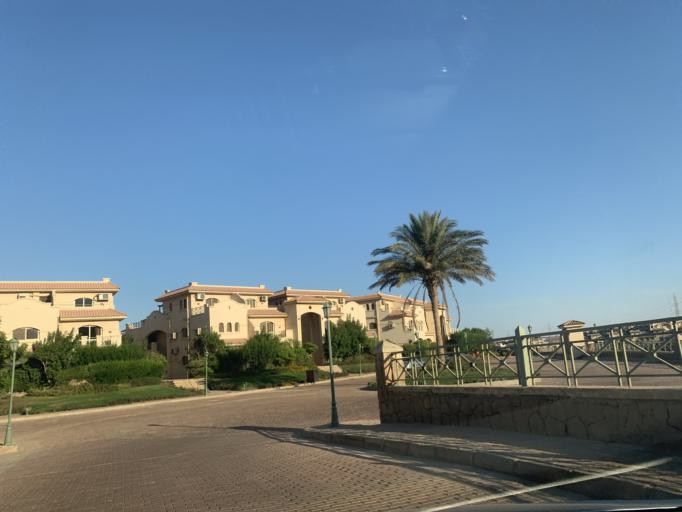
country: EG
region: As Suways
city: Ain Sukhna
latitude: 29.3719
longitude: 32.5690
